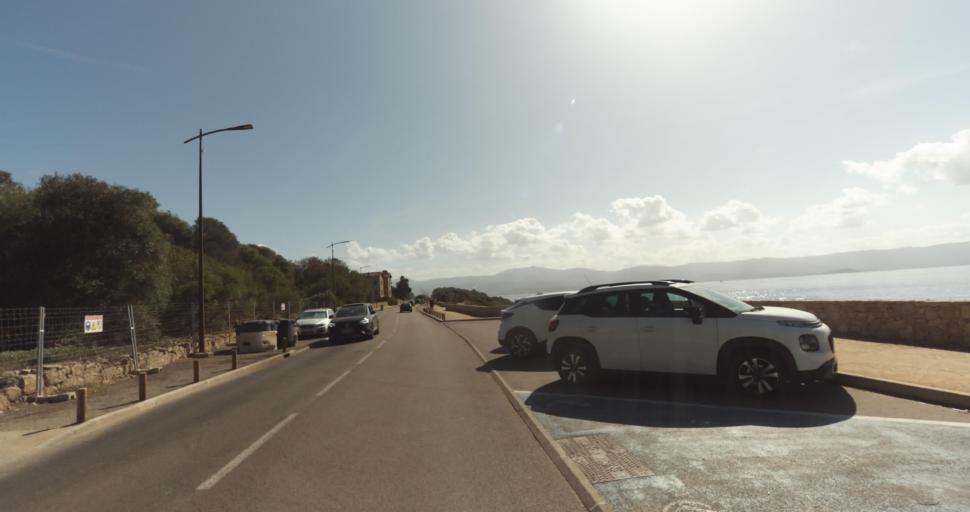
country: FR
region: Corsica
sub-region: Departement de la Corse-du-Sud
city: Ajaccio
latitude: 41.9094
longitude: 8.6910
